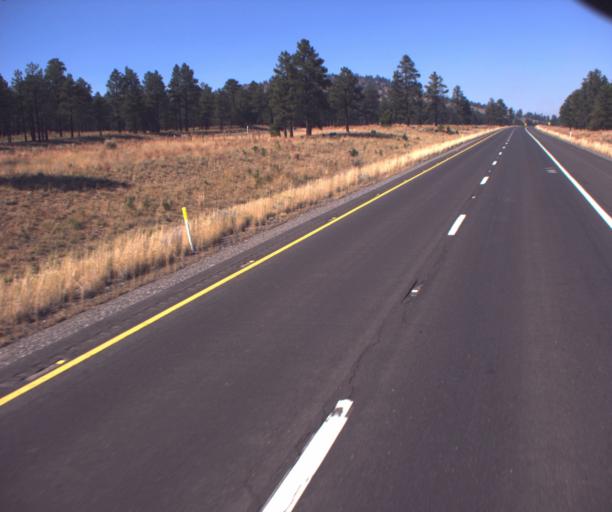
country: US
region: Arizona
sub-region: Coconino County
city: Flagstaff
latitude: 35.3746
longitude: -111.5767
